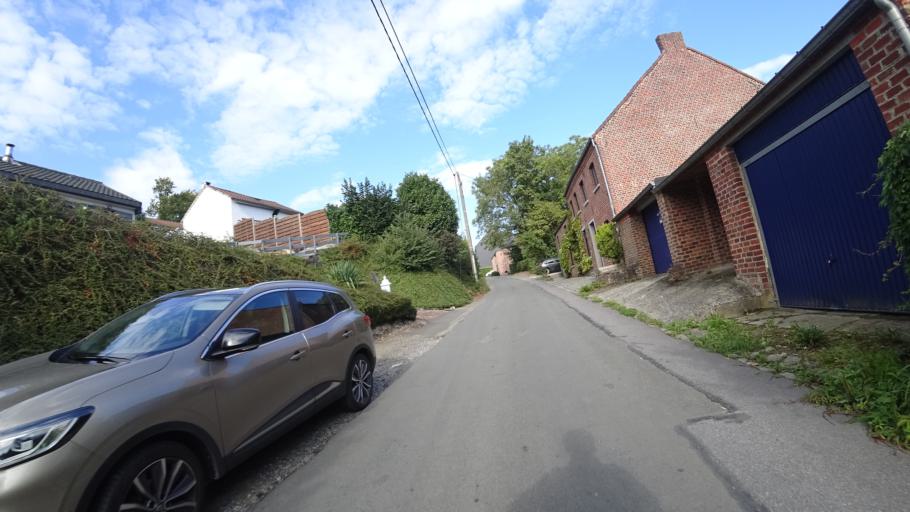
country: BE
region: Wallonia
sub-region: Province du Brabant Wallon
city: Villers-la-Ville
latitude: 50.6142
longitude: 4.5038
